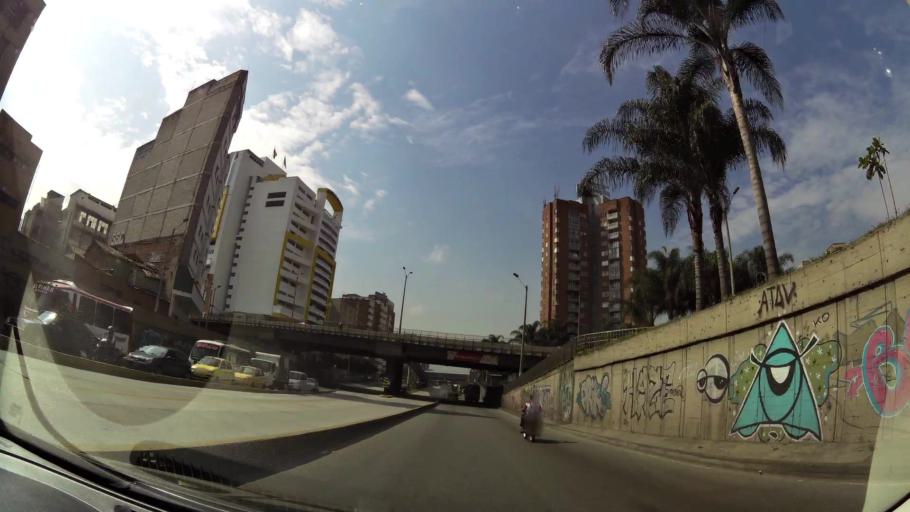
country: CO
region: Antioquia
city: Medellin
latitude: 6.2536
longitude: -75.5750
